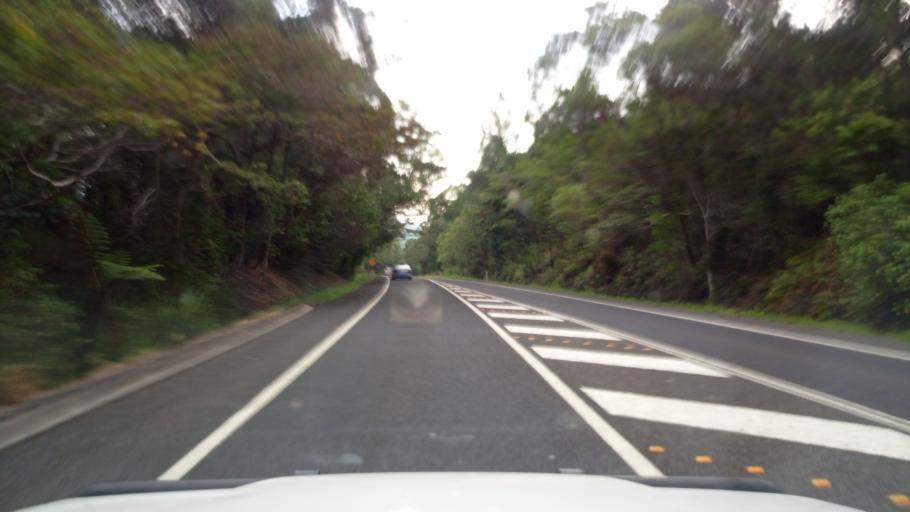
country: AU
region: Queensland
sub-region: Tablelands
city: Kuranda
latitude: -16.8336
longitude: 145.6198
